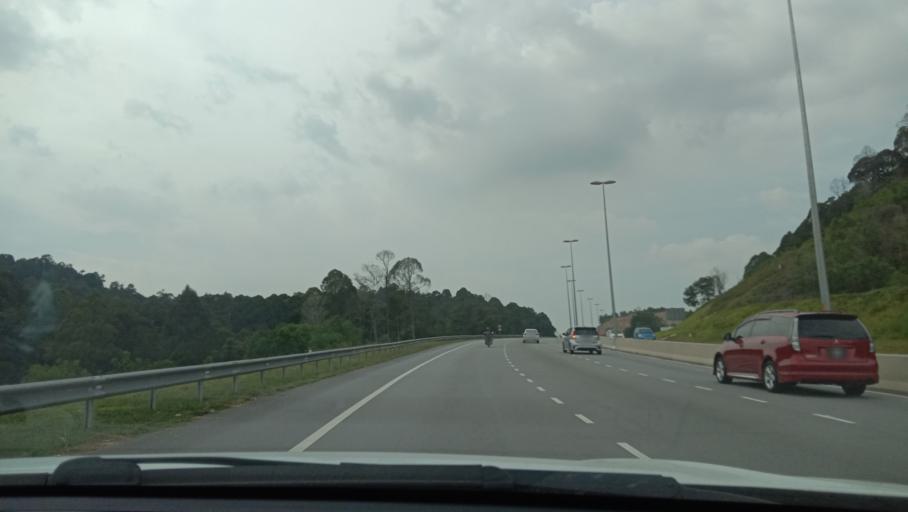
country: MY
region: Selangor
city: Kampung Baru Subang
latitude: 3.1265
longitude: 101.5142
